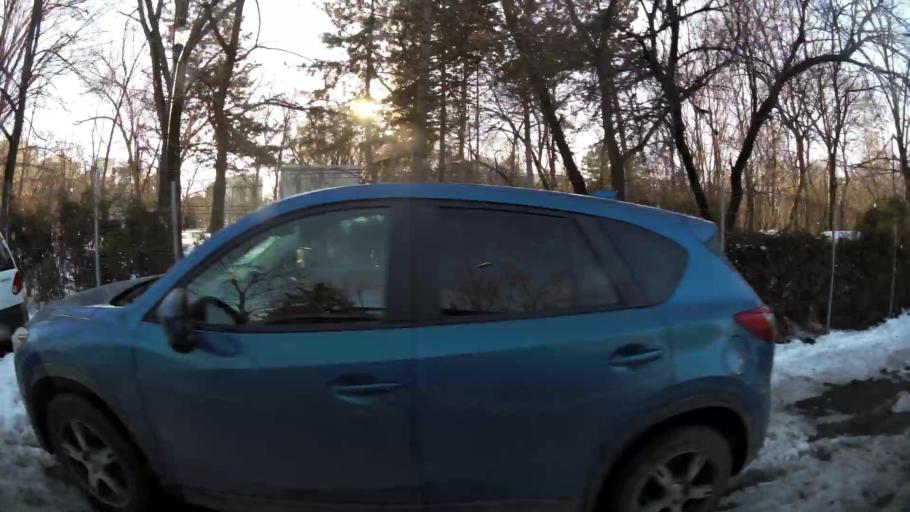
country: RO
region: Ilfov
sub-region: Comuna Fundeni-Dobroesti
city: Fundeni
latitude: 44.4653
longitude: 26.1340
